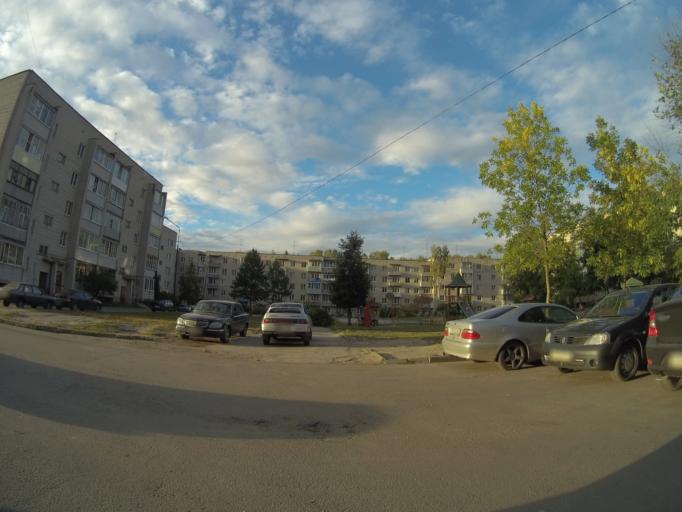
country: RU
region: Vladimir
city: Vladimir
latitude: 56.1108
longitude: 40.2791
